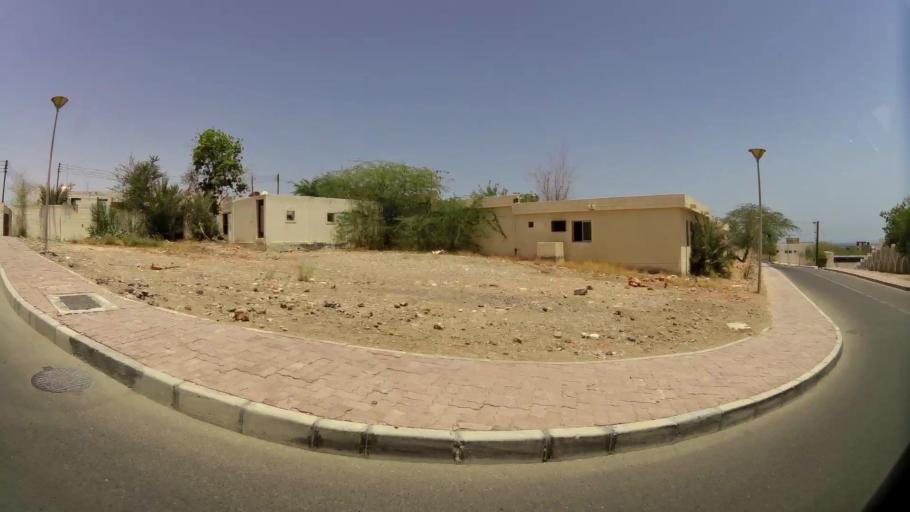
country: OM
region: Muhafazat Masqat
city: Bawshar
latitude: 23.6089
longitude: 58.4682
